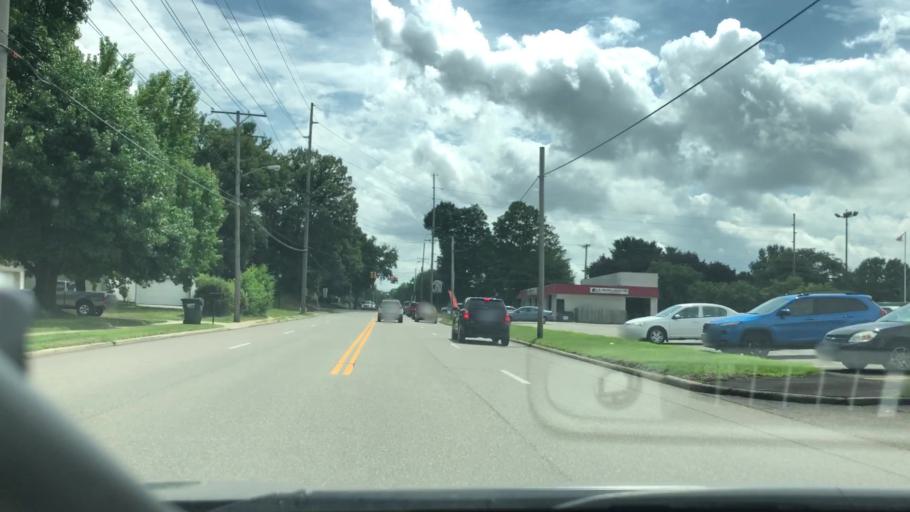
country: US
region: Ohio
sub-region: Stark County
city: Massillon
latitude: 40.8140
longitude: -81.5166
